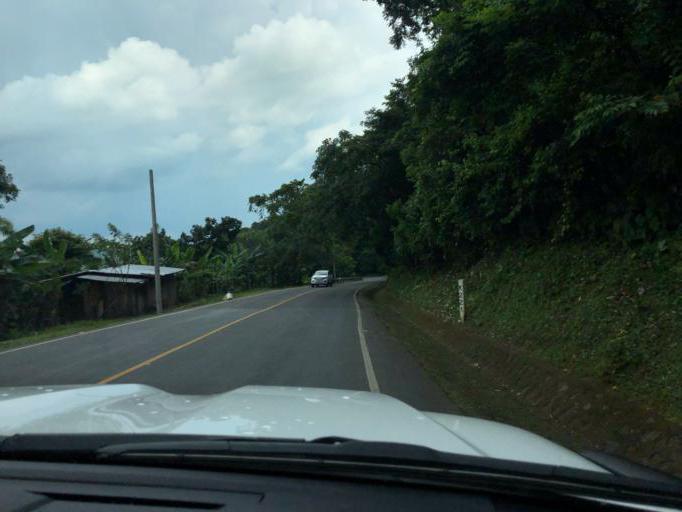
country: NI
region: Chontales
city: Villa Sandino
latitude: 12.0010
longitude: -84.7708
